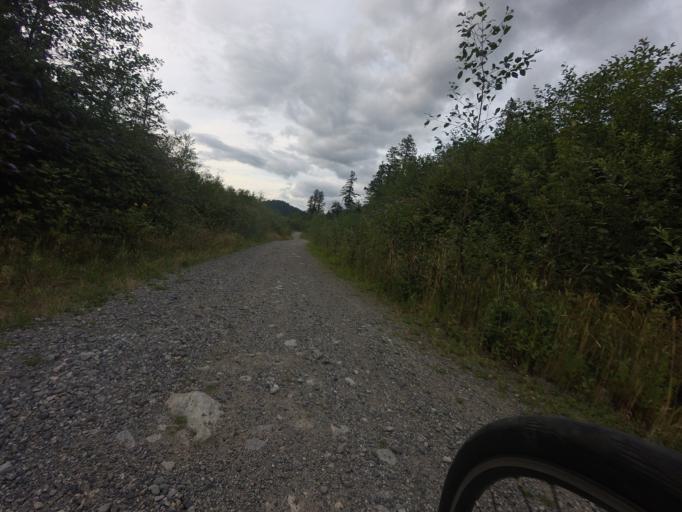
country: CA
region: British Columbia
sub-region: Greater Vancouver Regional District
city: Lions Bay
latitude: 49.5797
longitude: -123.2271
